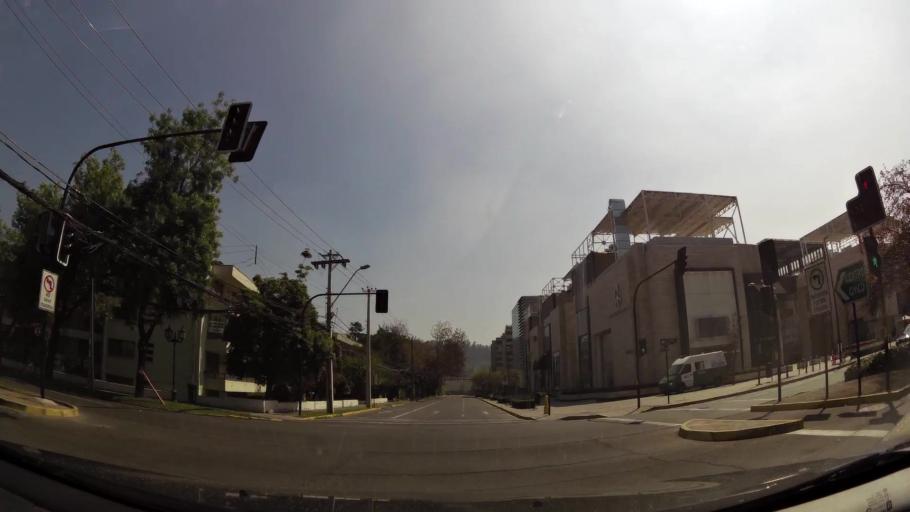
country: CL
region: Santiago Metropolitan
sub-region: Provincia de Santiago
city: Villa Presidente Frei, Nunoa, Santiago, Chile
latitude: -33.3991
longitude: -70.5979
